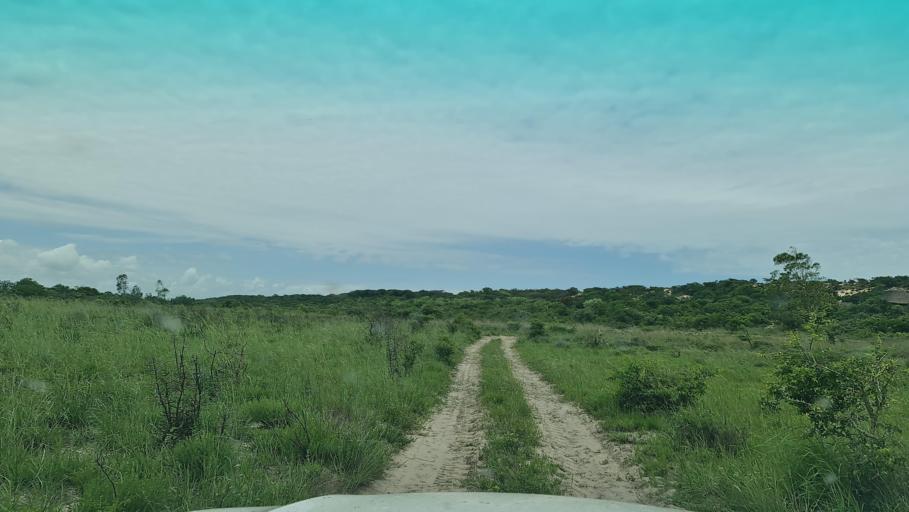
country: MZ
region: Maputo
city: Manhica
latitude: -25.6373
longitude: 32.7731
